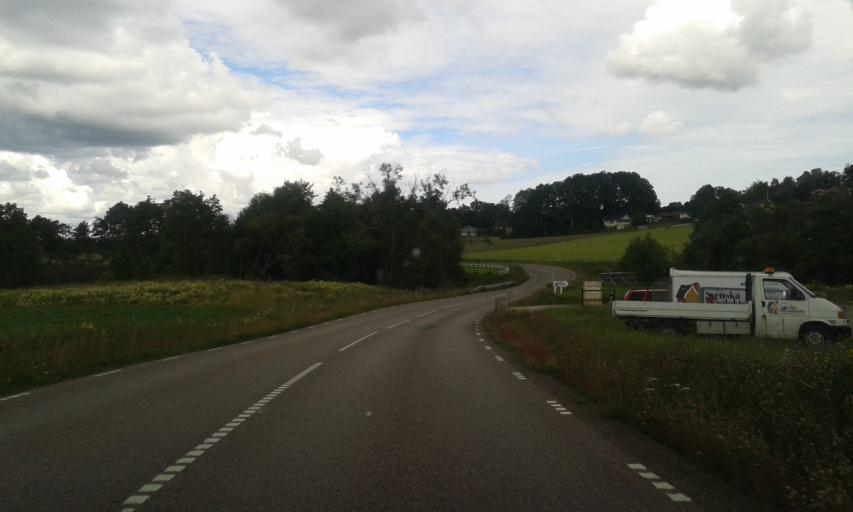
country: SE
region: Vaestra Goetaland
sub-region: Lilla Edets Kommun
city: Lilla Edet
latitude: 58.1156
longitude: 12.1148
